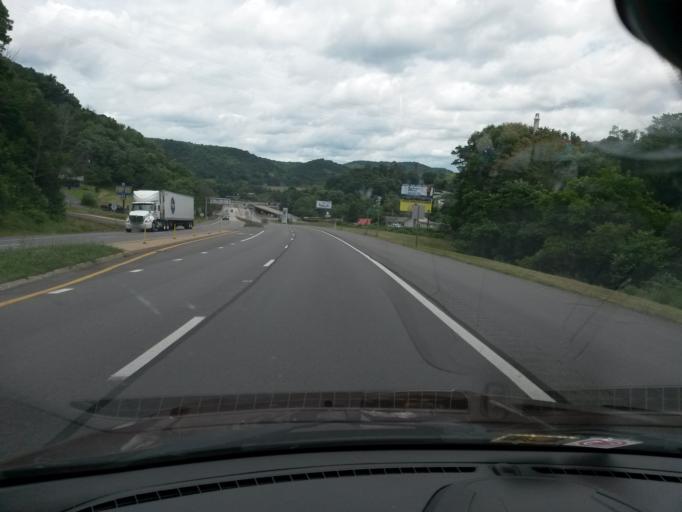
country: US
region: Virginia
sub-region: Giles County
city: Narrows
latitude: 37.3656
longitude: -80.8695
